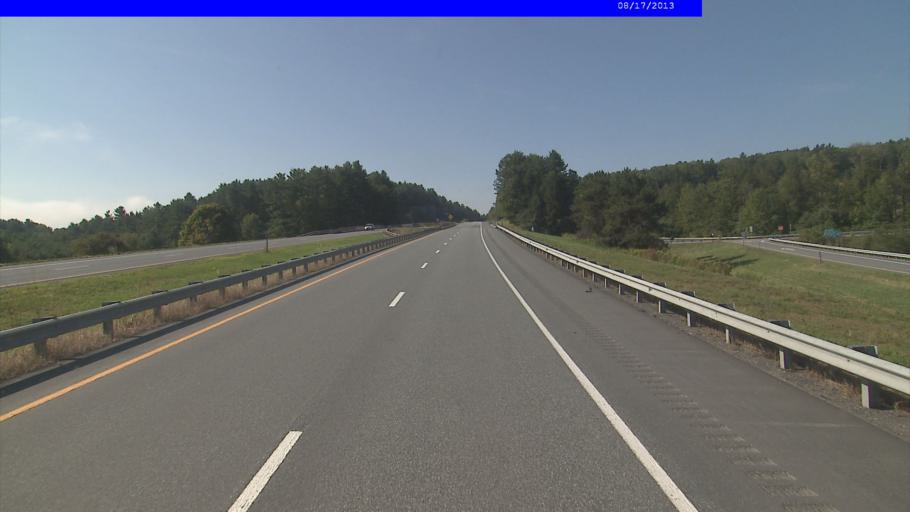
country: US
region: Vermont
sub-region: Windsor County
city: Wilder
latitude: 43.6679
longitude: -72.3188
